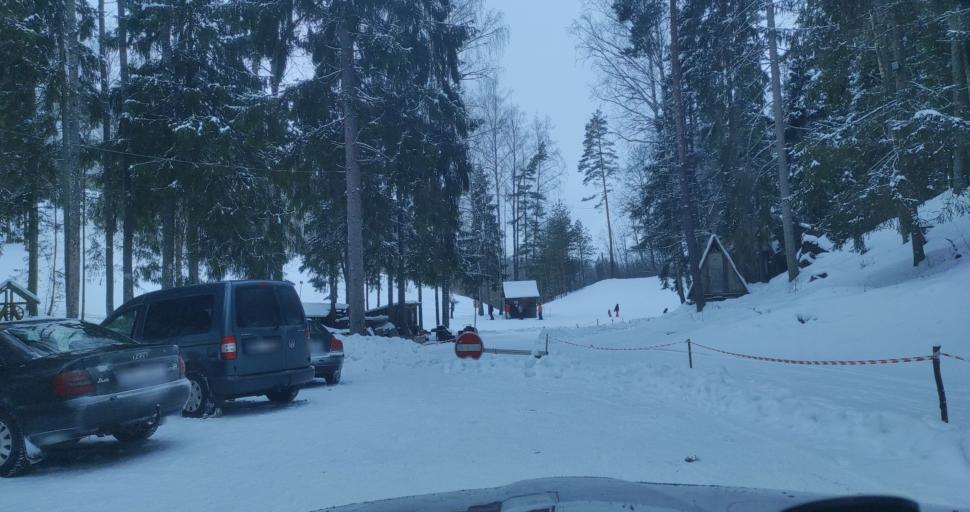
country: LV
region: Plavinu
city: Plavinas
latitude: 56.6541
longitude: 25.7401
